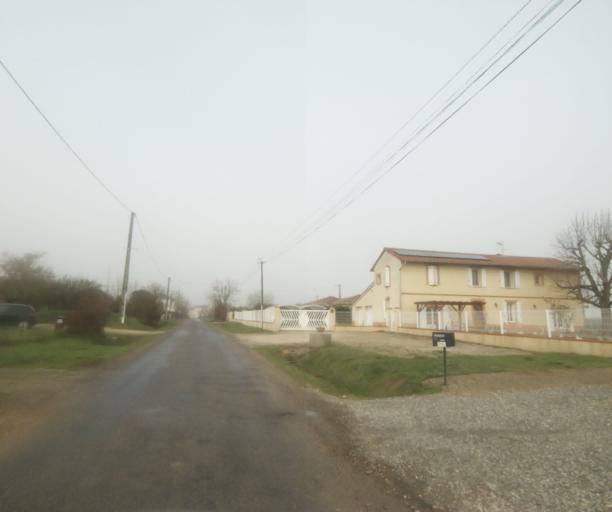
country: FR
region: Midi-Pyrenees
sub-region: Departement de la Haute-Garonne
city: Villaudric
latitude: 43.8358
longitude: 1.4639
